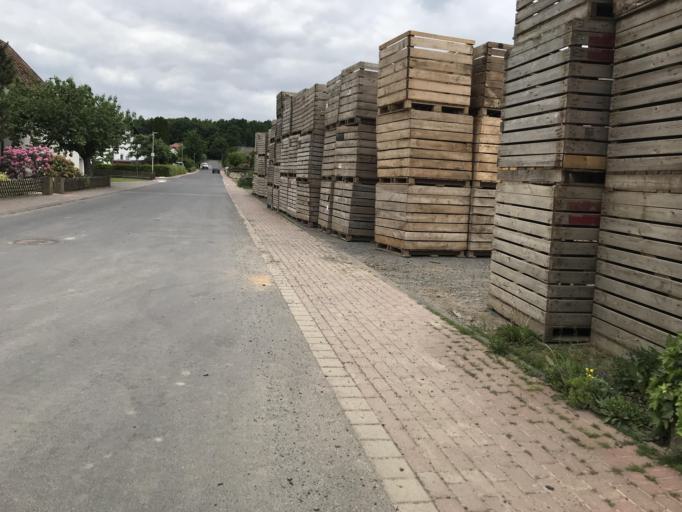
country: DE
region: Hesse
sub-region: Regierungsbezirk Kassel
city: Martinhagen
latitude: 51.2885
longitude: 9.2833
